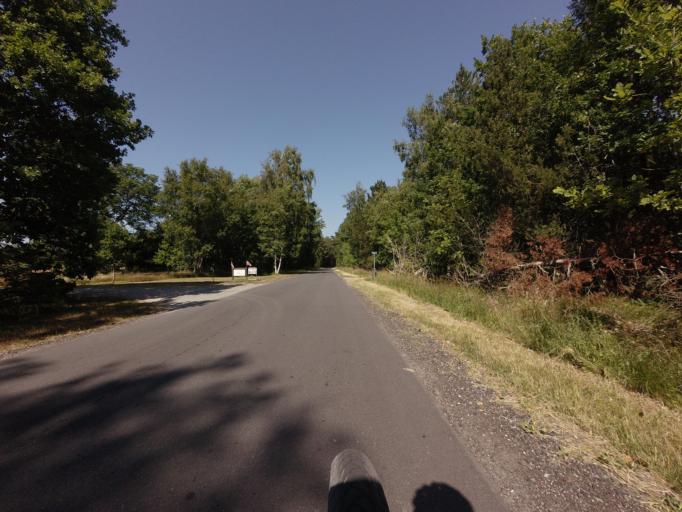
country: DK
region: North Denmark
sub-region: Laeso Kommune
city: Byrum
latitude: 57.2650
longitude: 11.0024
